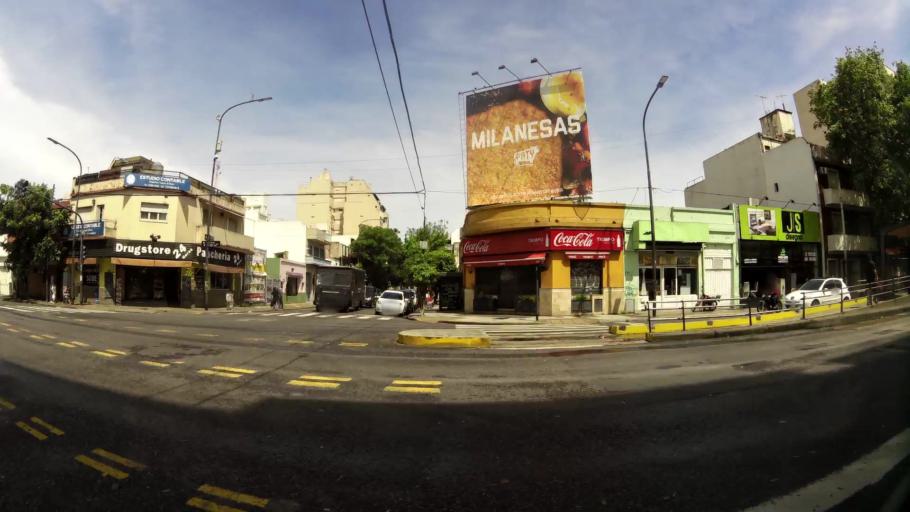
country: AR
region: Buenos Aires F.D.
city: Villa Santa Rita
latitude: -34.6113
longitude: -58.4680
